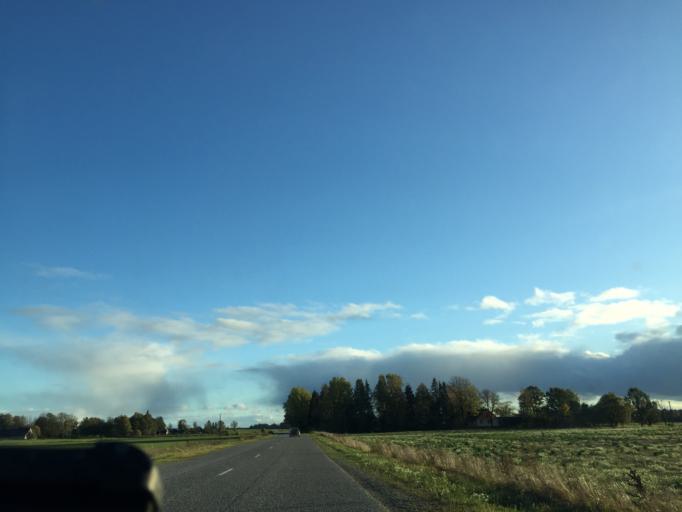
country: LV
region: Saldus Rajons
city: Saldus
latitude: 56.8207
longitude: 22.3777
